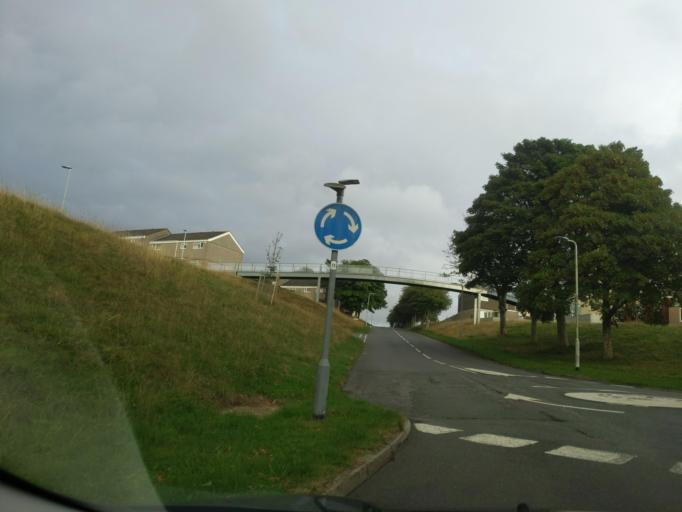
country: GB
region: England
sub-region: Devon
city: Plympton
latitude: 50.4040
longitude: -4.0996
